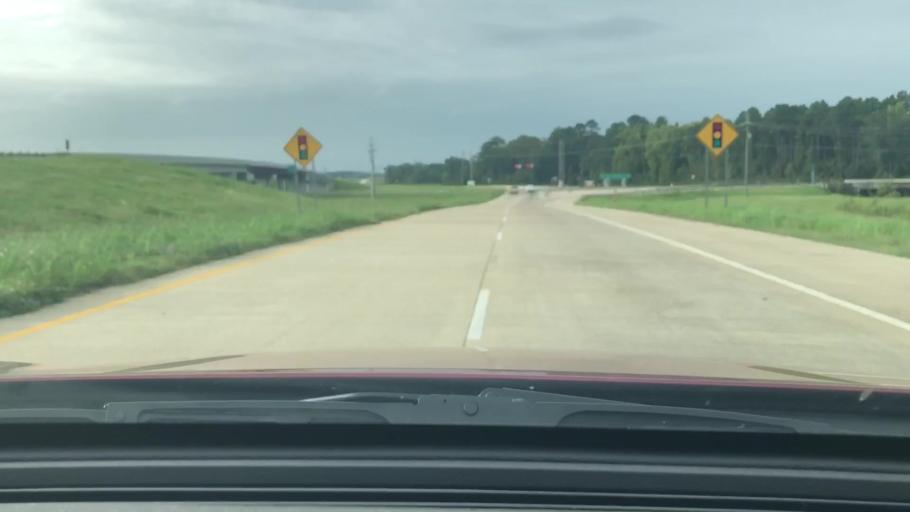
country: US
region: Louisiana
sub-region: Caddo Parish
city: Blanchard
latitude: 32.5986
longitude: -93.8329
